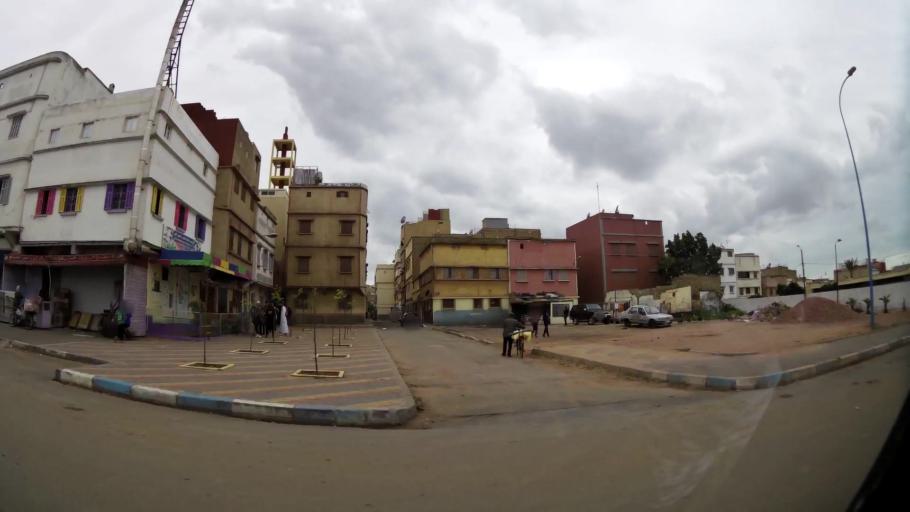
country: MA
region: Grand Casablanca
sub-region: Casablanca
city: Casablanca
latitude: 33.5691
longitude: -7.5666
